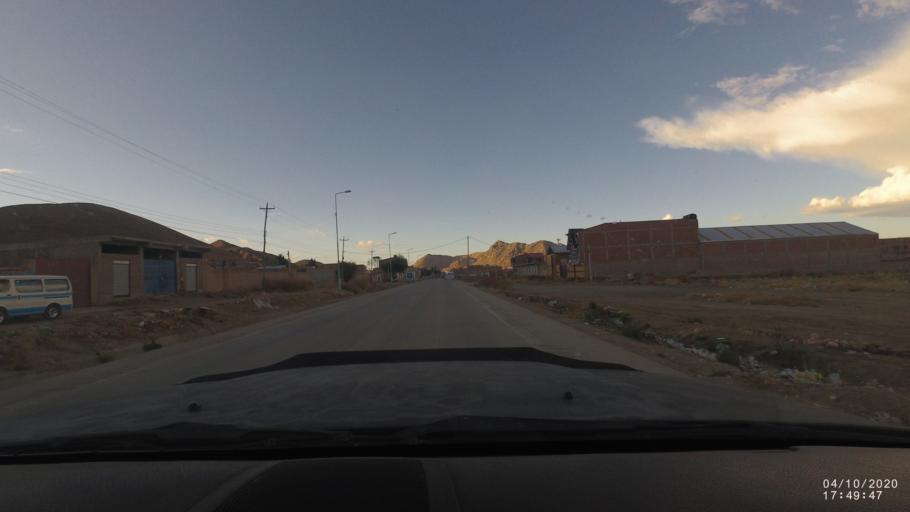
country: BO
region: Oruro
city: Oruro
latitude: -18.0070
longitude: -67.1362
